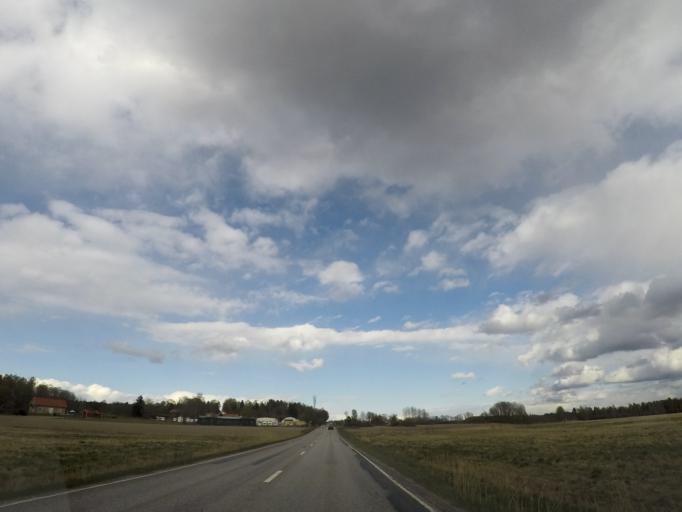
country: SE
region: Soedermanland
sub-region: Eskilstuna Kommun
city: Hallbybrunn
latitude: 59.3215
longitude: 16.3931
